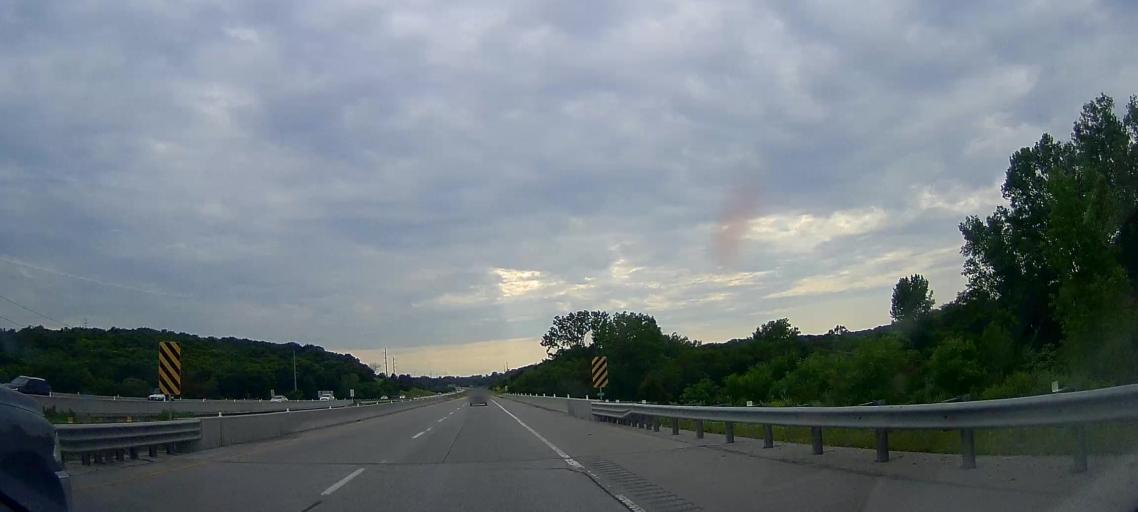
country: US
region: Iowa
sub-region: Pottawattamie County
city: Carter Lake
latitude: 41.3471
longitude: -95.9934
